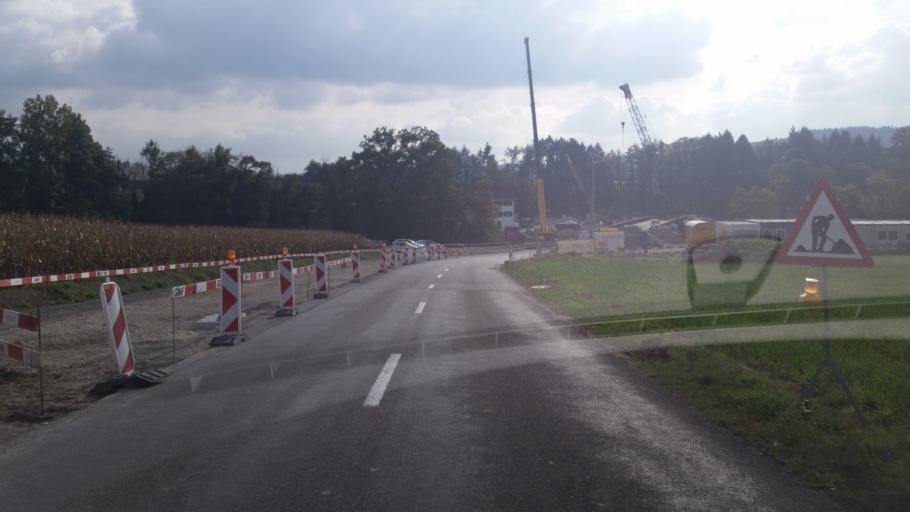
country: CH
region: Aargau
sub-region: Bezirk Baden
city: Niederrohrdorf
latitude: 47.3957
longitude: 8.3037
